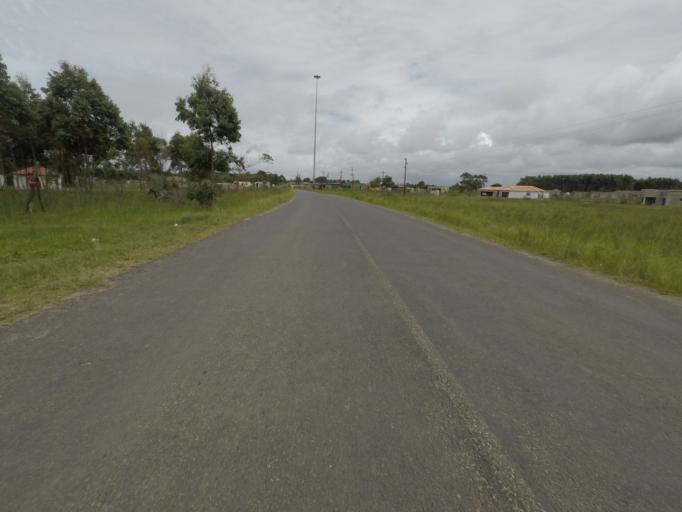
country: ZA
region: KwaZulu-Natal
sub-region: uThungulu District Municipality
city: eSikhawini
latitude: -28.9109
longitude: 31.8655
